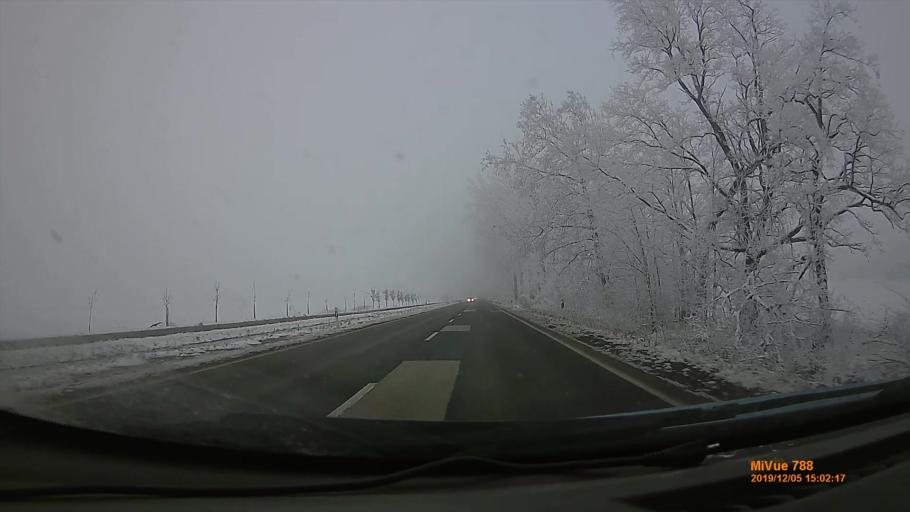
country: HU
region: Szabolcs-Szatmar-Bereg
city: Tiszanagyfalu
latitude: 48.0745
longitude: 21.5164
